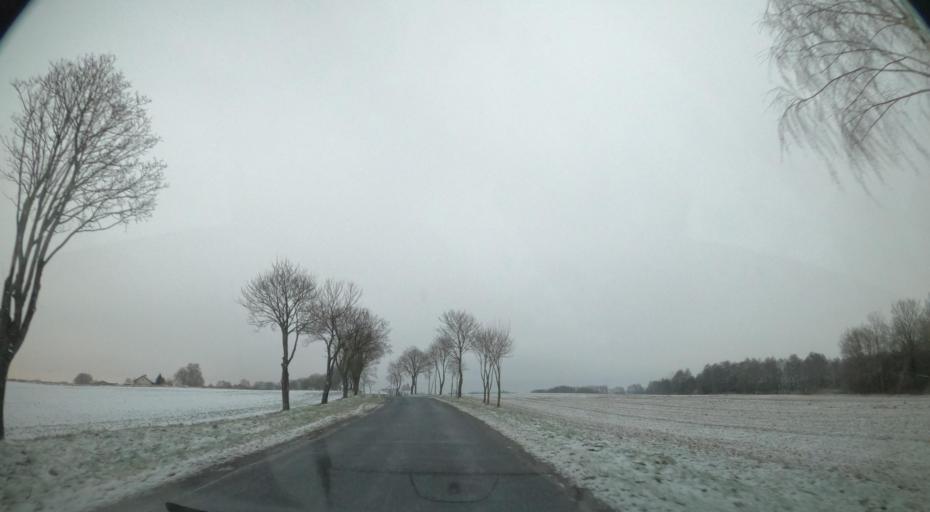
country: PL
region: Kujawsko-Pomorskie
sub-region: Powiat lipnowski
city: Wielgie
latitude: 52.7034
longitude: 19.2883
